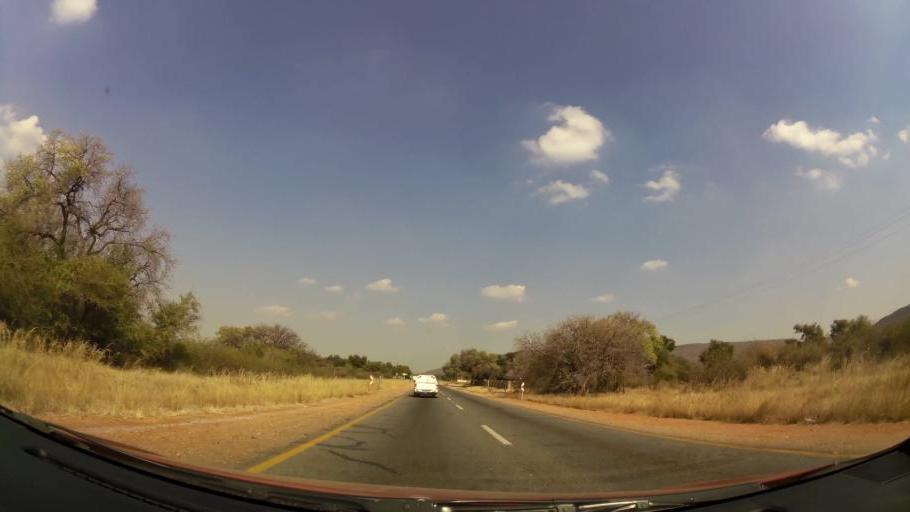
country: ZA
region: North-West
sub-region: Bojanala Platinum District Municipality
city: Rustenburg
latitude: -25.4833
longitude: 27.0863
